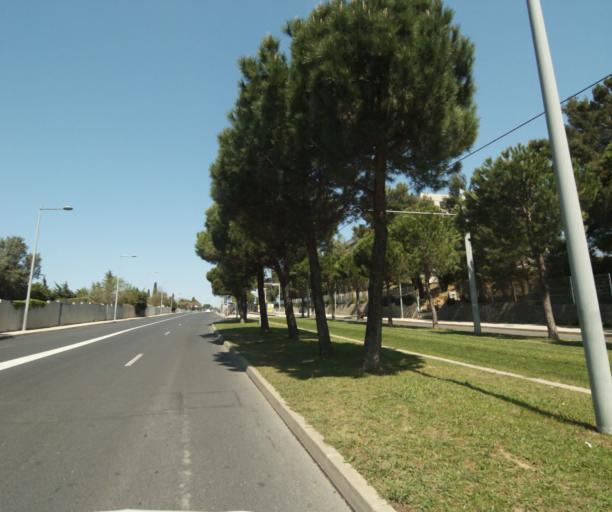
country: FR
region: Languedoc-Roussillon
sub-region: Departement de l'Herault
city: Juvignac
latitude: 43.6354
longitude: 3.8226
